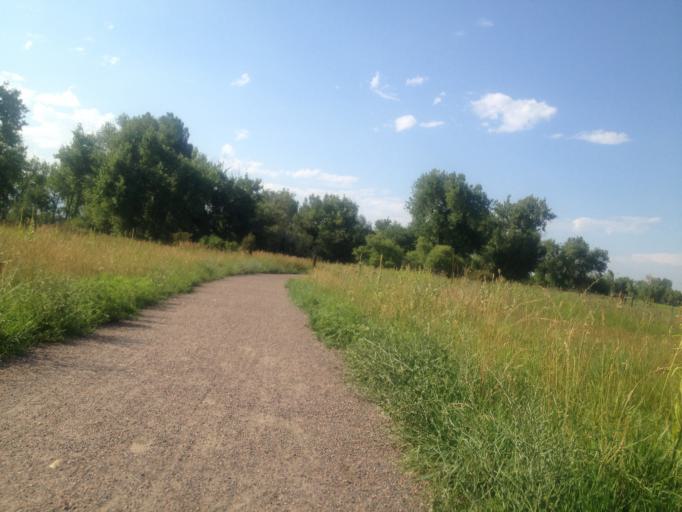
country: US
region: Colorado
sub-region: Boulder County
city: Boulder
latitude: 39.9925
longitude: -105.2168
